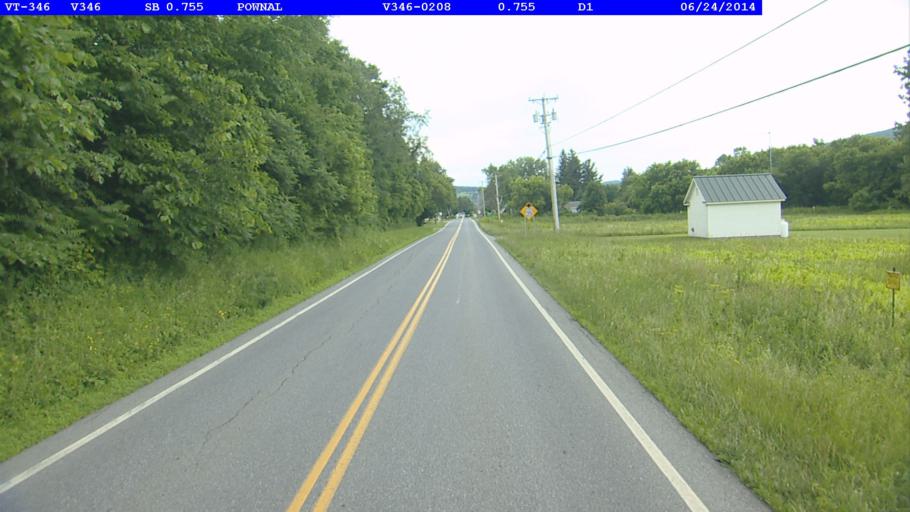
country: US
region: Massachusetts
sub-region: Berkshire County
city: Williamstown
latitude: 42.7717
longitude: -73.2403
